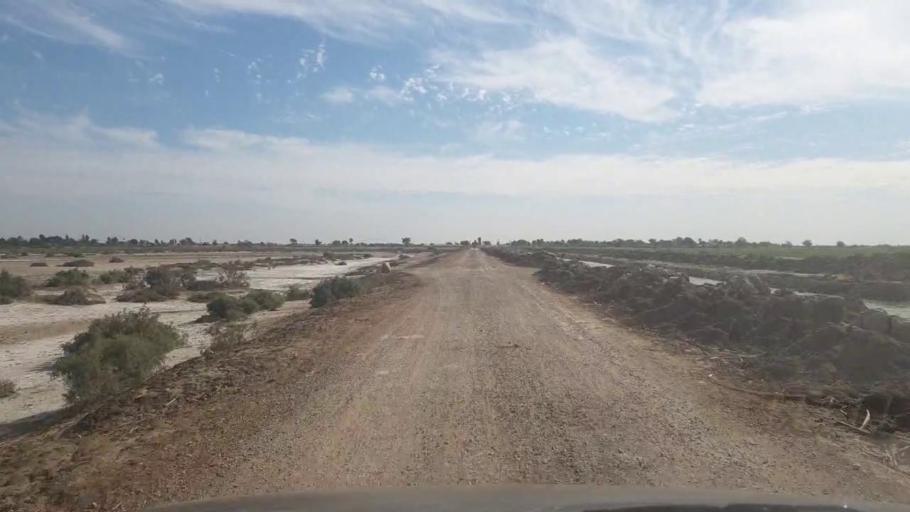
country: PK
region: Sindh
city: Mirwah Gorchani
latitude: 25.4250
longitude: 69.2006
